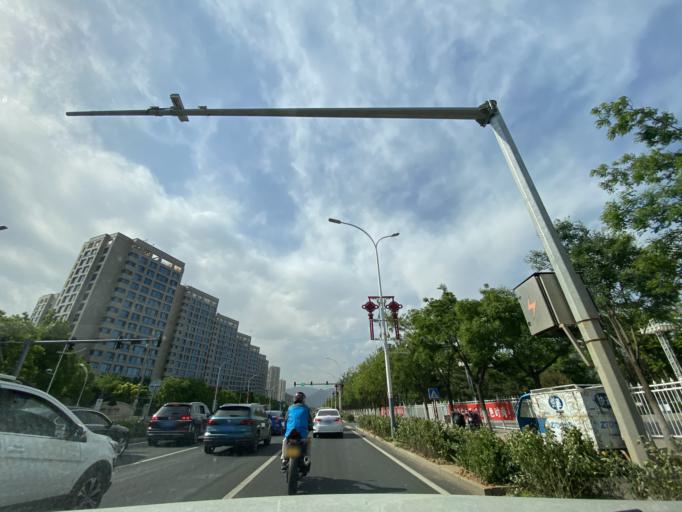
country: CN
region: Beijing
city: Dayu
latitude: 39.9473
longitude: 116.0999
